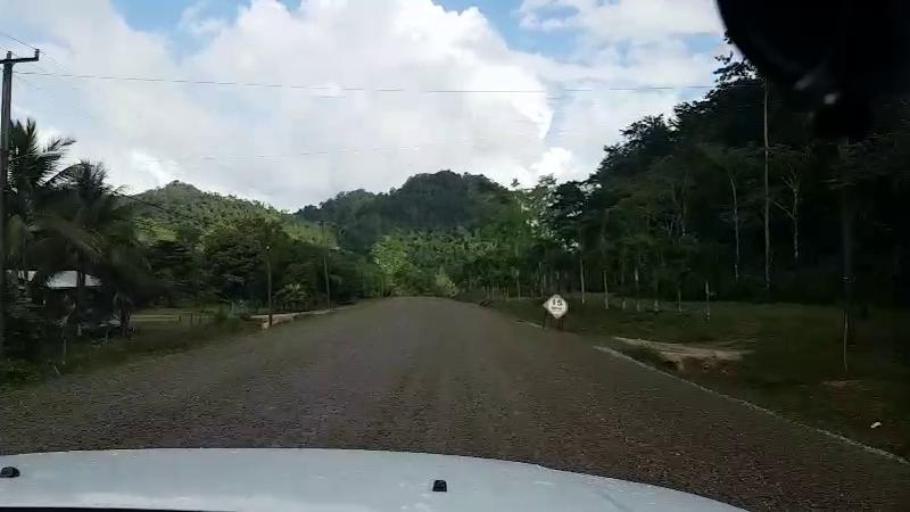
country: BZ
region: Cayo
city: Belmopan
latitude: 17.0913
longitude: -88.6279
